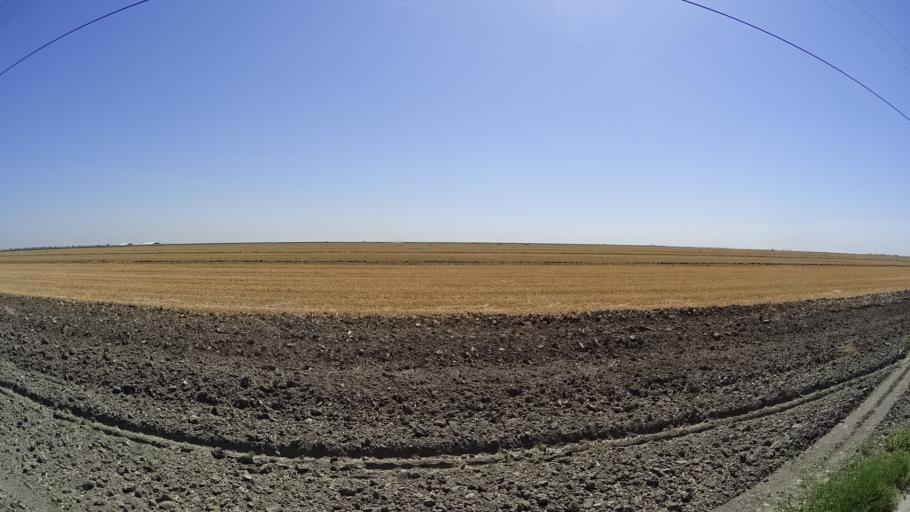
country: US
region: California
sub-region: Kings County
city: Corcoran
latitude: 36.0164
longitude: -119.5361
